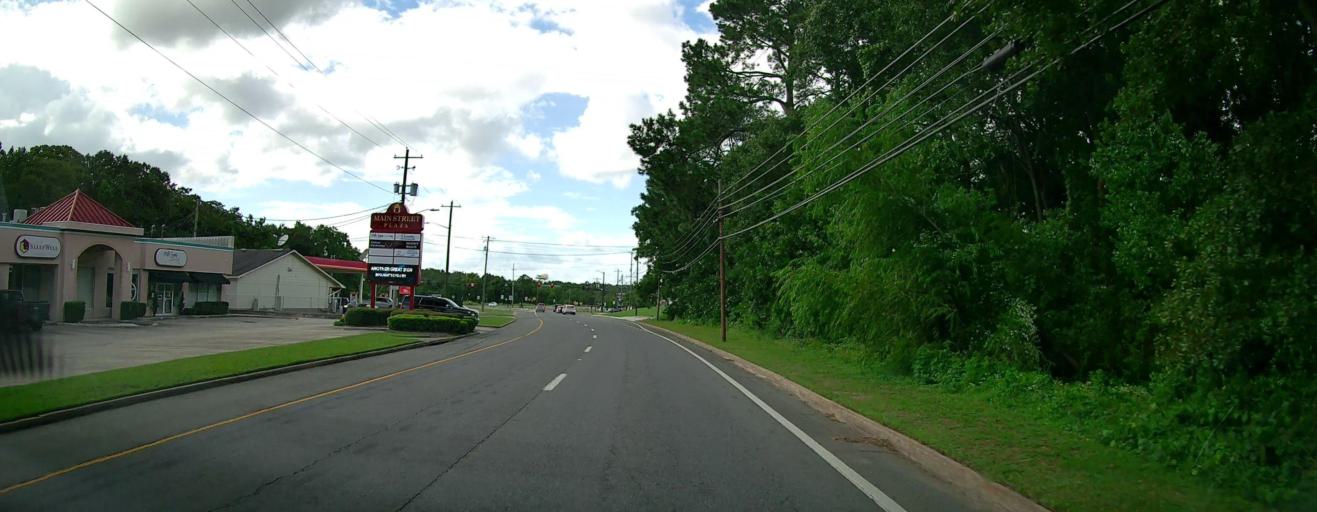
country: US
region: Georgia
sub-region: Coffee County
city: Douglas
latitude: 31.5245
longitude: -82.8495
